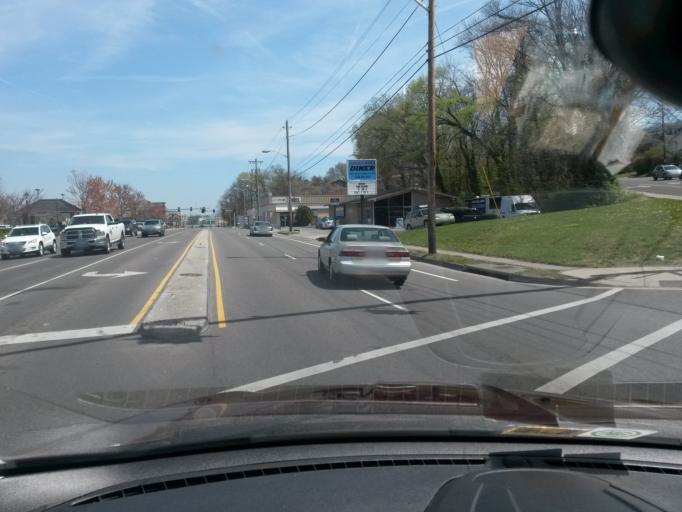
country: US
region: Virginia
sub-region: City of Roanoke
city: Cedar Bluff
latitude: 37.2494
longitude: -79.9562
